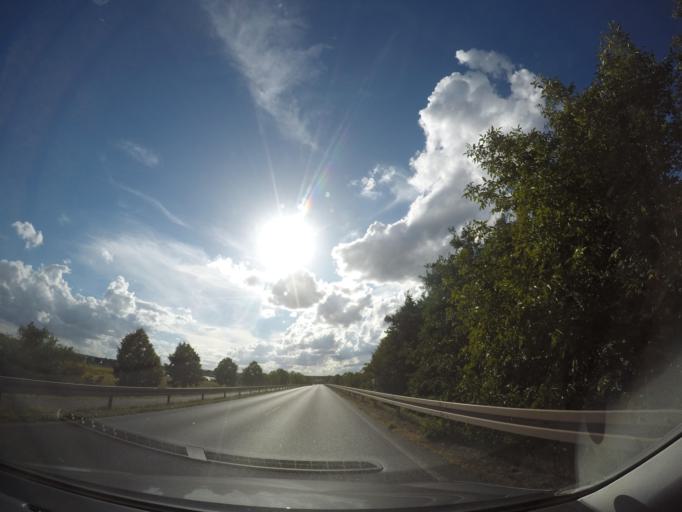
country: DE
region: Saxony-Anhalt
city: Haldensleben I
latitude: 52.3013
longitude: 11.4037
